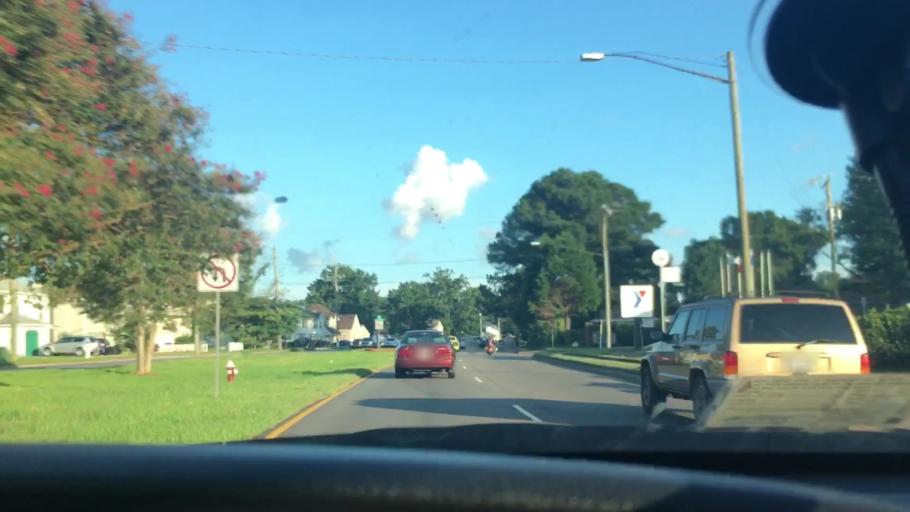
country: US
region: Virginia
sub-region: City of Norfolk
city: Norfolk
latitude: 36.8927
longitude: -76.1403
